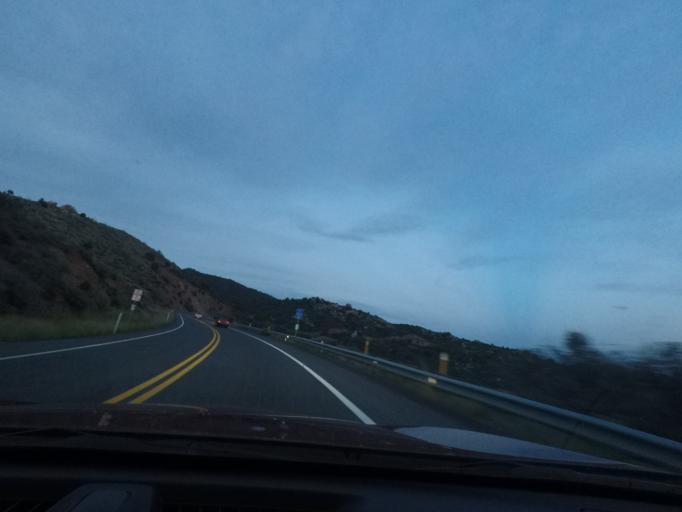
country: US
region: Arizona
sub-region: Yavapai County
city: Williamson
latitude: 34.5918
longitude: -112.5871
